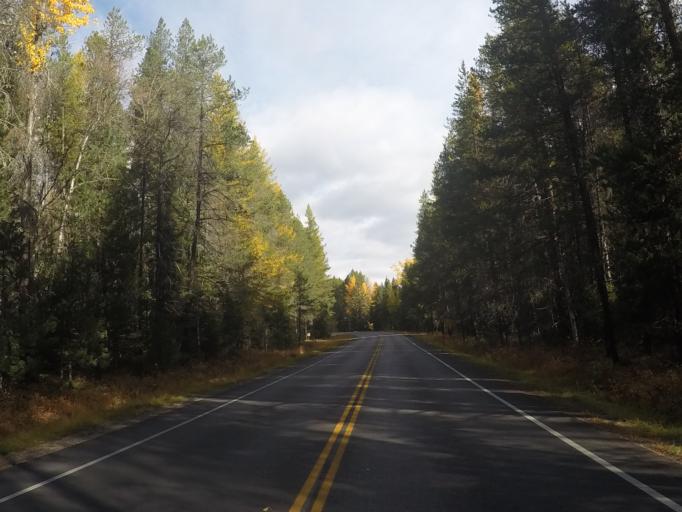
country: US
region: Montana
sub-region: Flathead County
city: Columbia Falls
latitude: 48.5081
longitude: -113.9869
